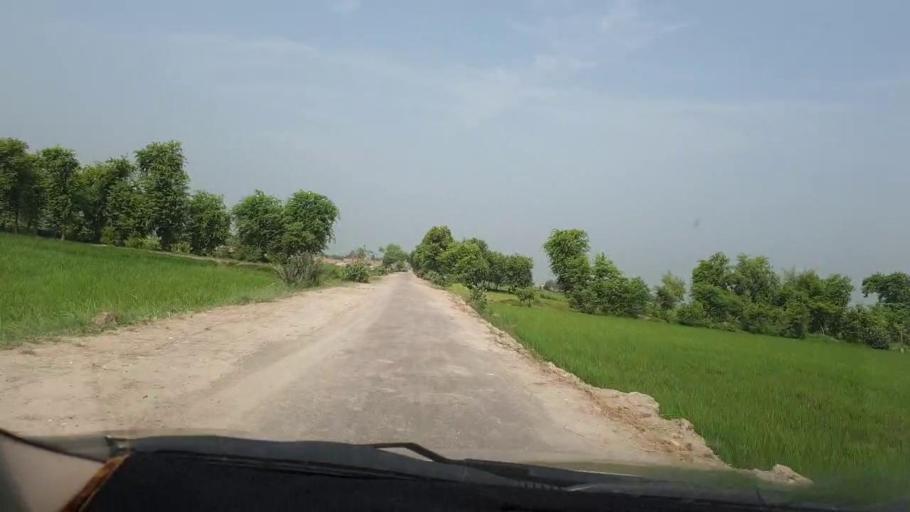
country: PK
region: Sindh
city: Goth Garelo
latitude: 27.4843
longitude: 68.0454
